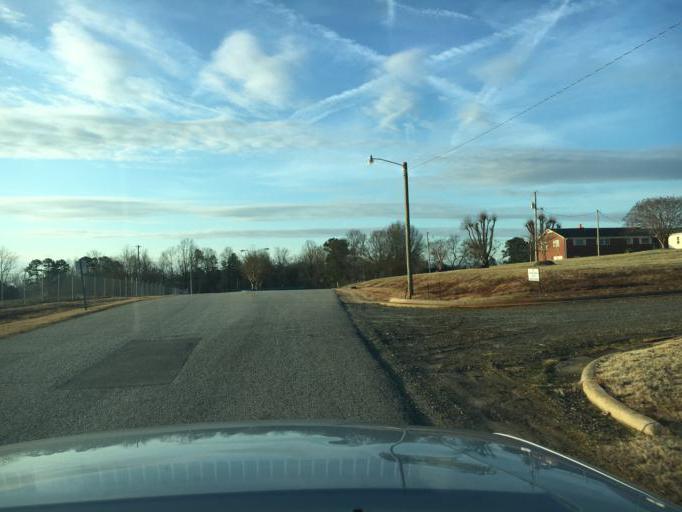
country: US
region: North Carolina
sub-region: Catawba County
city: Maiden
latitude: 35.5972
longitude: -81.2508
